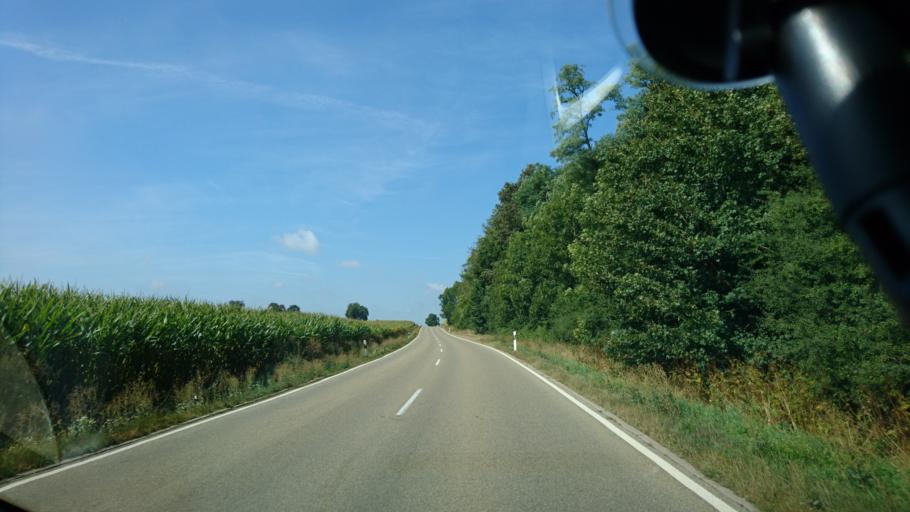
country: DE
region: Baden-Wuerttemberg
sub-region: Regierungsbezirk Stuttgart
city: Ilshofen
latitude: 49.1668
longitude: 9.8923
